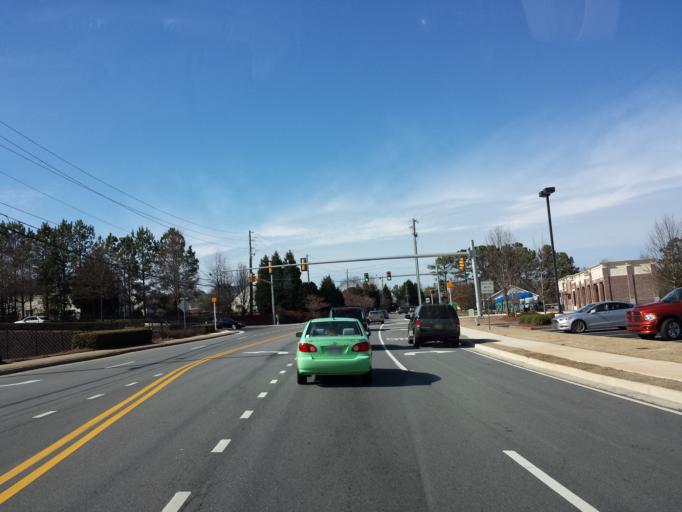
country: US
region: Georgia
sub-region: Cobb County
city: Kennesaw
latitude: 33.9941
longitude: -84.5980
